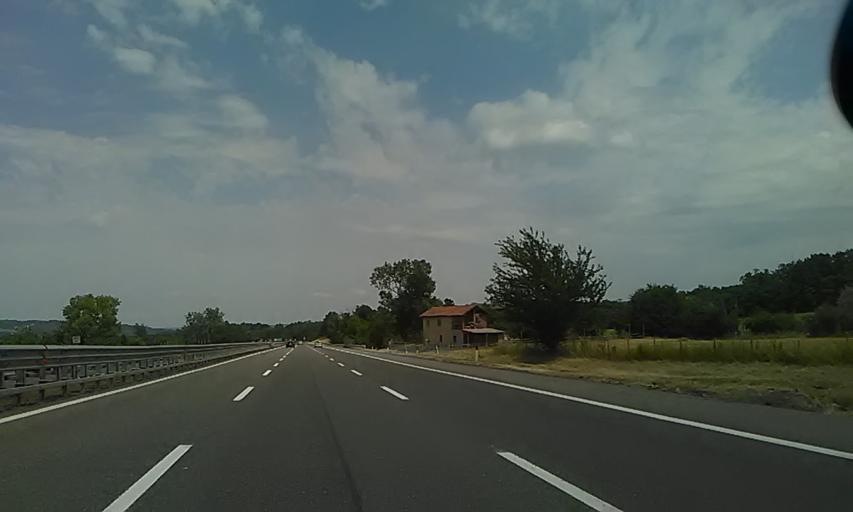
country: IT
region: Piedmont
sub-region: Provincia di Alessandria
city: Tagliolo Monferrato
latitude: 44.6452
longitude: 8.6609
